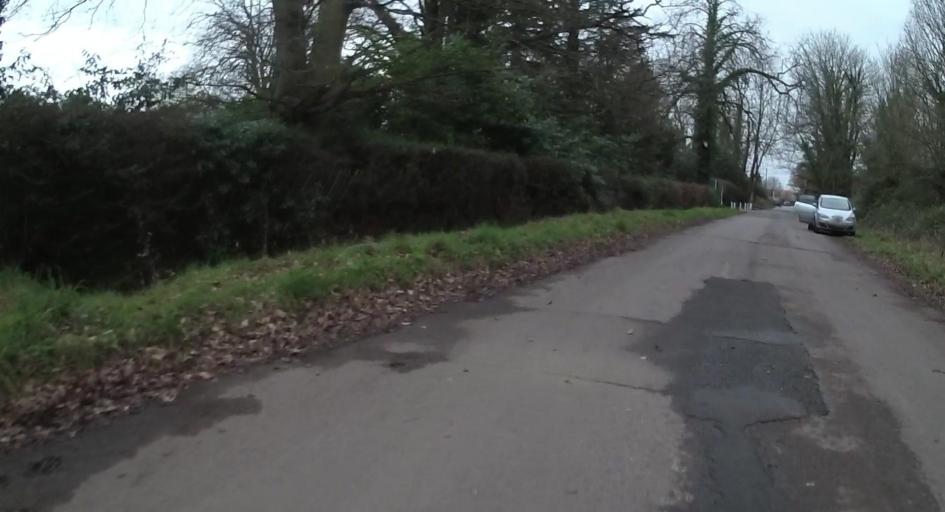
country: GB
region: England
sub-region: Wokingham
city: Shinfield
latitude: 51.4142
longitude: -0.9370
